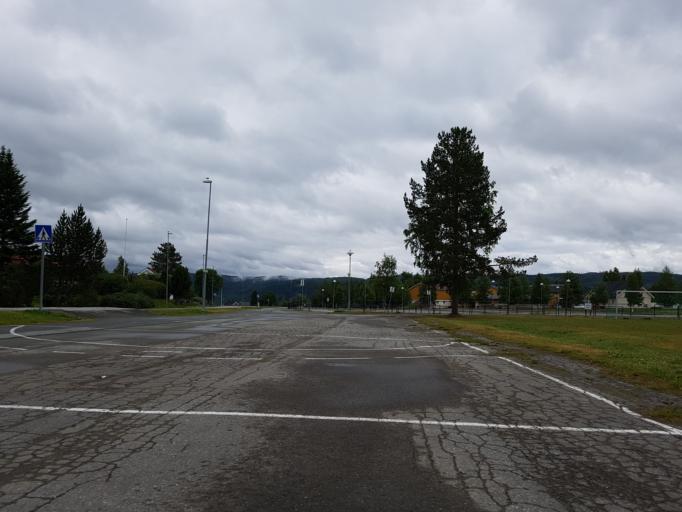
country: NO
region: Sor-Trondelag
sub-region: Selbu
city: Mebonden
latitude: 63.2266
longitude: 11.0334
